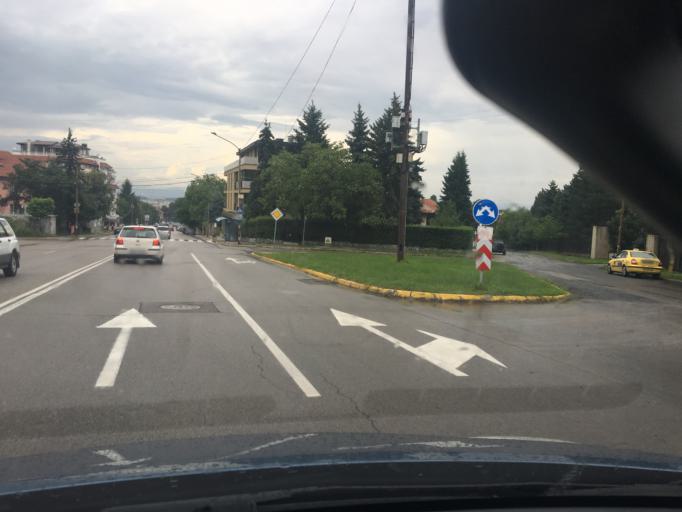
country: BG
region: Sofia-Capital
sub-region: Stolichna Obshtina
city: Sofia
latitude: 42.6549
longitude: 23.2657
